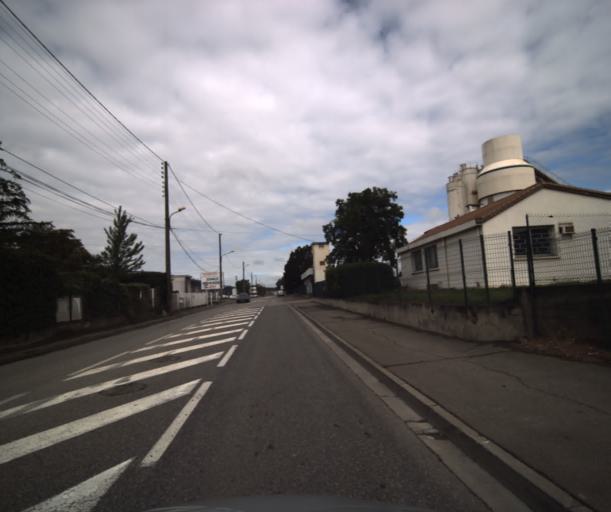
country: FR
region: Midi-Pyrenees
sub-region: Departement de la Haute-Garonne
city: Portet-sur-Garonne
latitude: 43.5492
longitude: 1.4154
